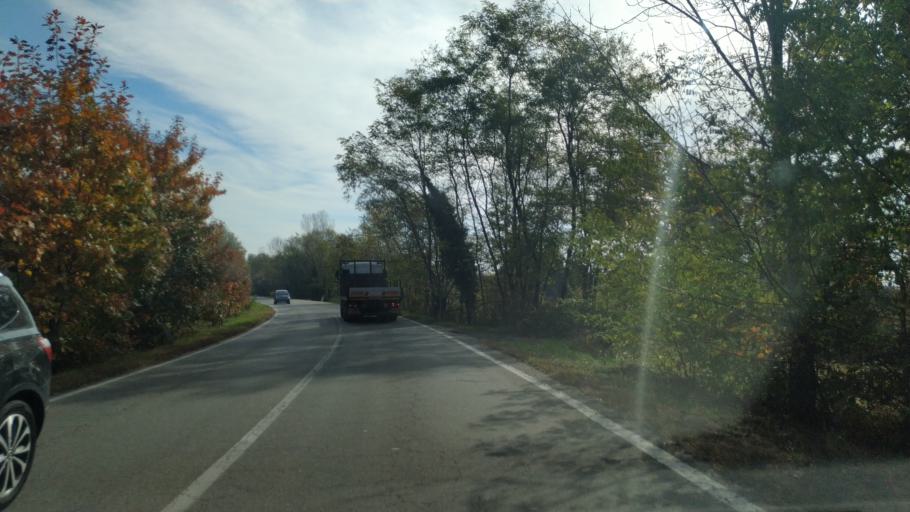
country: IT
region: Piedmont
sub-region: Provincia di Novara
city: Romagnano Sesia
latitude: 45.6391
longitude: 8.3966
